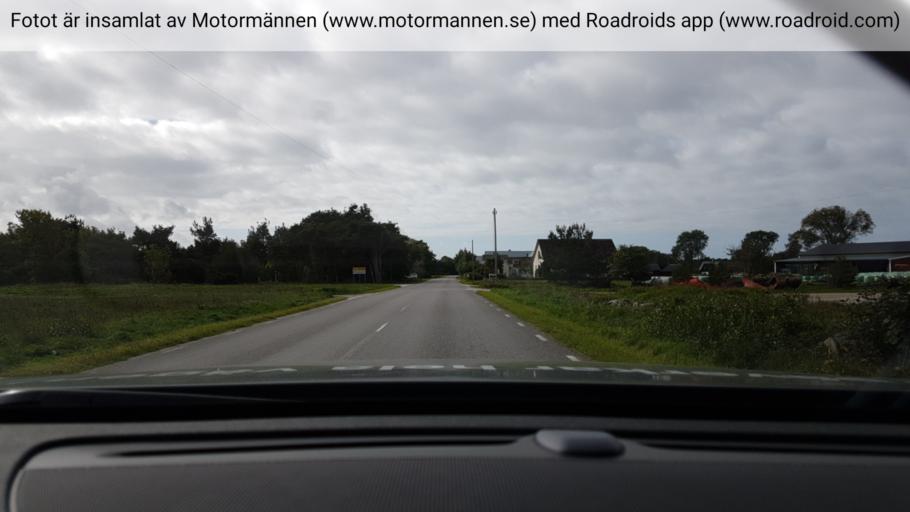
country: SE
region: Gotland
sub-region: Gotland
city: Hemse
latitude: 56.9667
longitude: 18.2284
